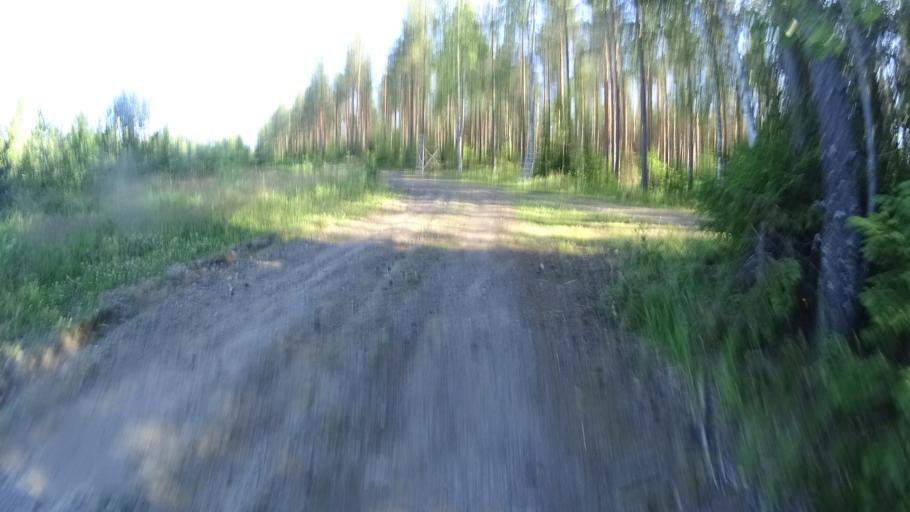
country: FI
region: Uusimaa
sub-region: Helsinki
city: Karkkila
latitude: 60.6580
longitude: 24.1313
